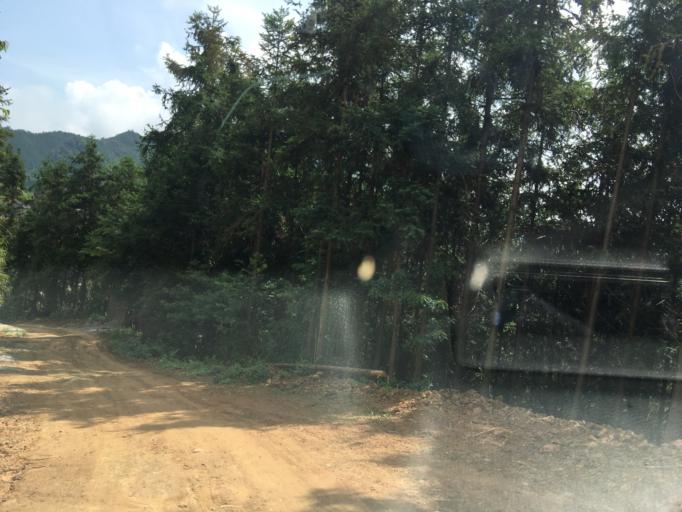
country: CN
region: Guangxi Zhuangzu Zizhiqu
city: Xinzhou
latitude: 24.8664
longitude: 105.8565
